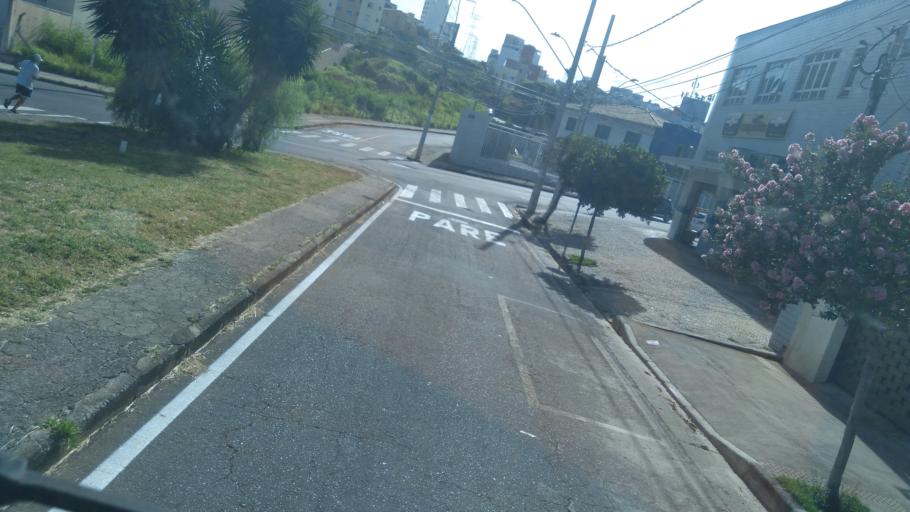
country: BR
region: Minas Gerais
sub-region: Belo Horizonte
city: Belo Horizonte
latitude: -19.8735
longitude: -43.9216
